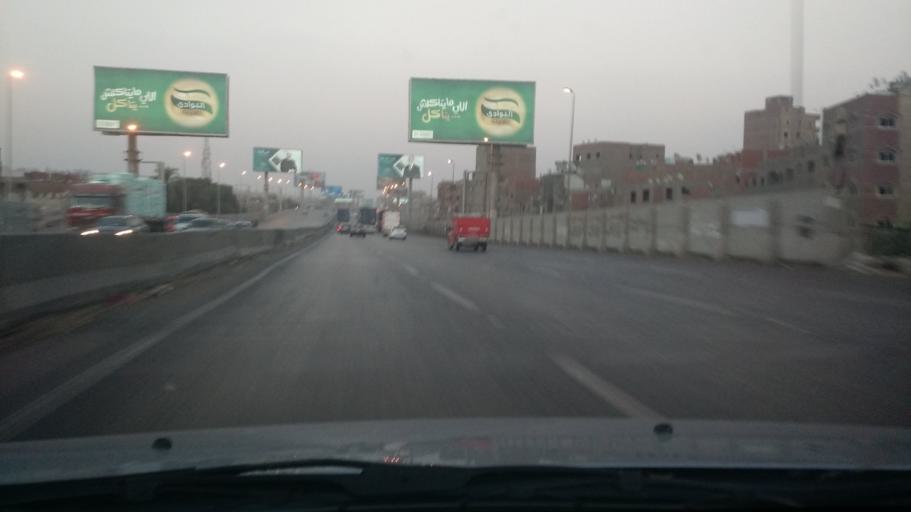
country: EG
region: Al Jizah
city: Al Jizah
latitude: 29.9899
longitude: 31.2619
